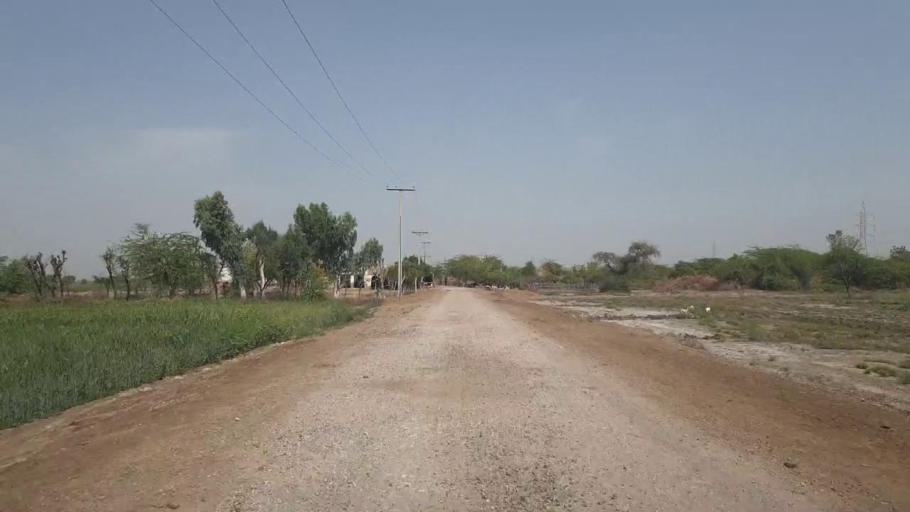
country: PK
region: Sindh
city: Umarkot
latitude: 25.3621
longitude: 69.6013
